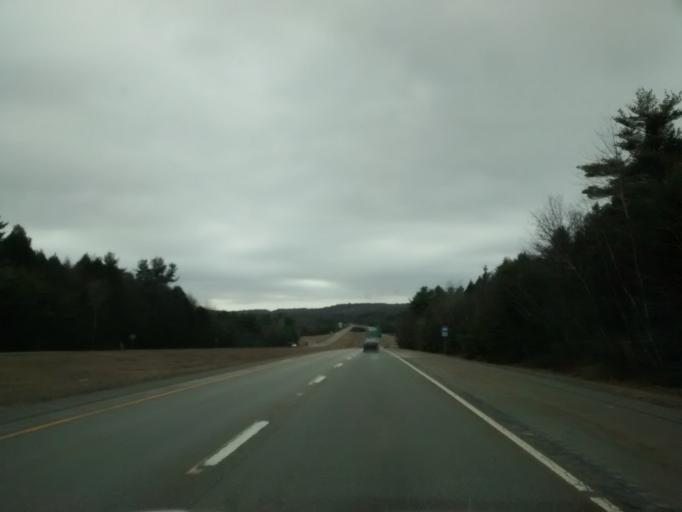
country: US
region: Massachusetts
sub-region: Worcester County
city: Phillipston
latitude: 42.5692
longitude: -72.1175
